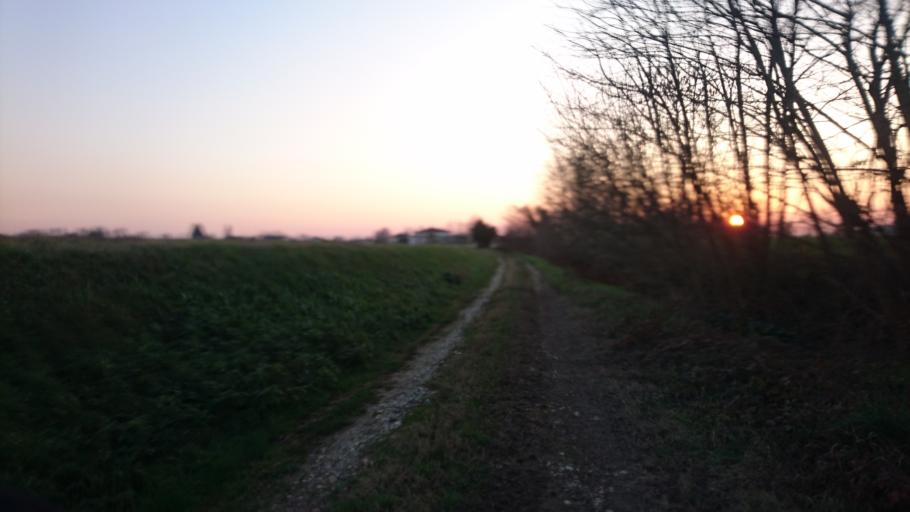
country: IT
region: Veneto
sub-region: Provincia di Padova
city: Villatora
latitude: 45.3741
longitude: 11.9593
